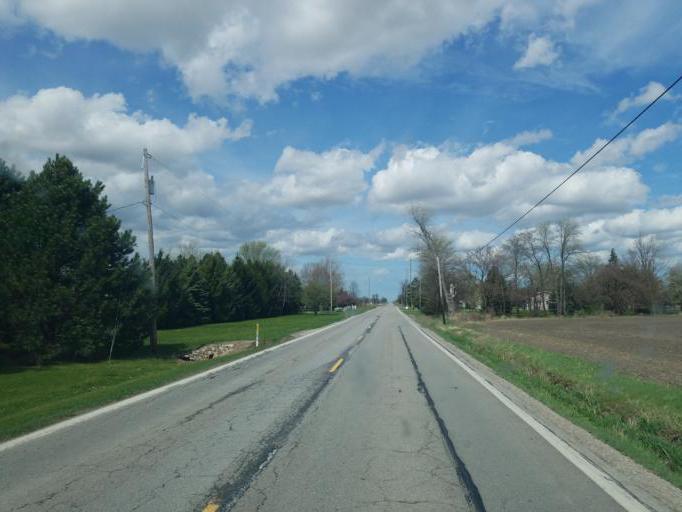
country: US
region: Ohio
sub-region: Huron County
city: Bellevue
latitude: 41.2708
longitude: -82.7922
